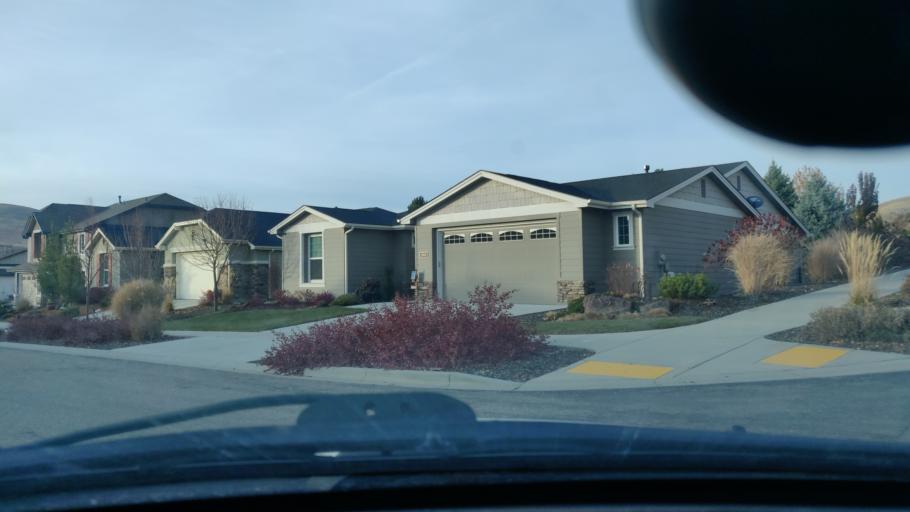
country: US
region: Idaho
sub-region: Ada County
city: Eagle
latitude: 43.7747
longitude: -116.2612
